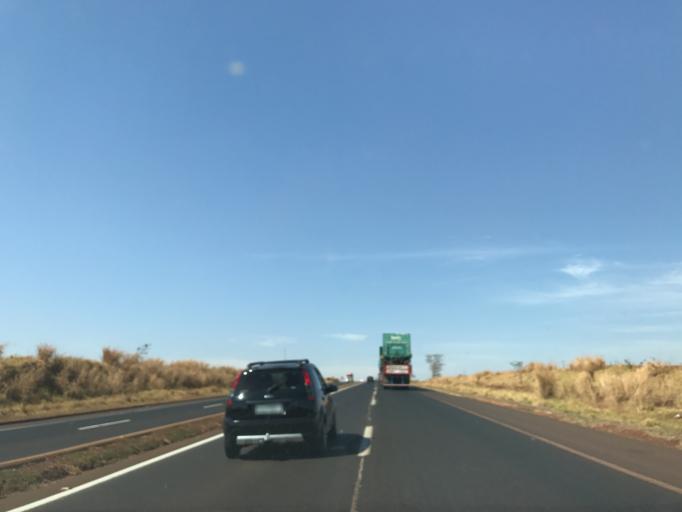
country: BR
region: Minas Gerais
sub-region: Centralina
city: Centralina
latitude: -18.5472
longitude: -49.1940
